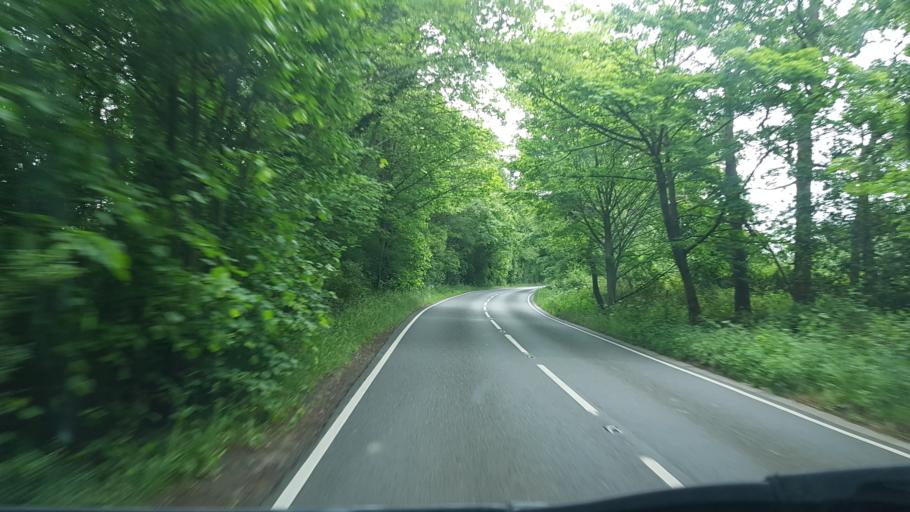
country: GB
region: England
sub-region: Surrey
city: East Horsley
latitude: 51.2923
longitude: -0.4550
